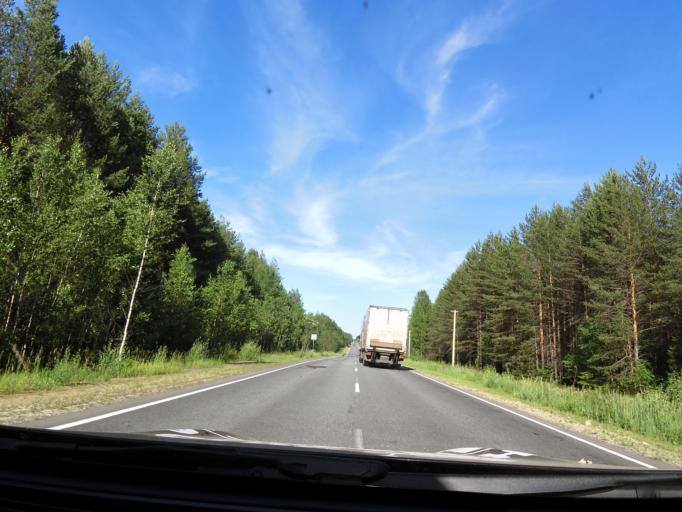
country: RU
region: Kirov
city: Belaya Kholunitsa
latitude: 58.9125
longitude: 51.0724
